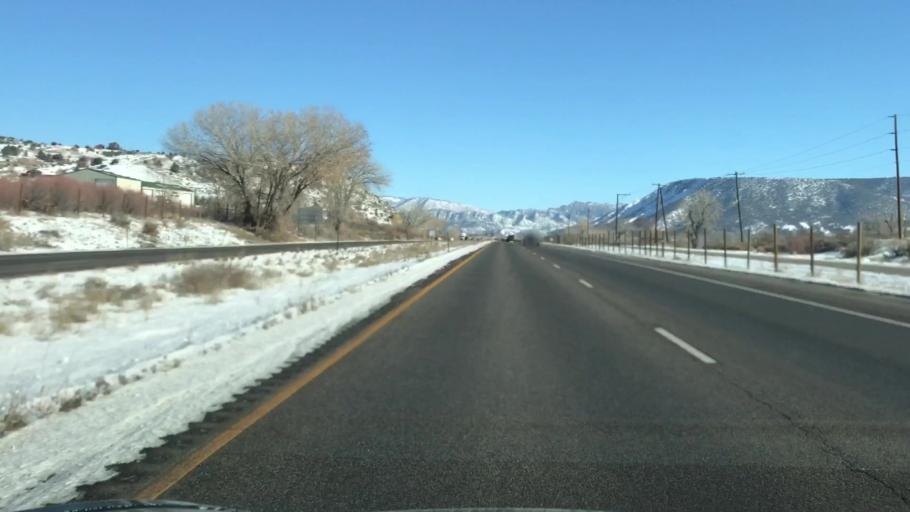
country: US
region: Colorado
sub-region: Garfield County
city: Silt
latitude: 39.5442
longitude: -107.6367
